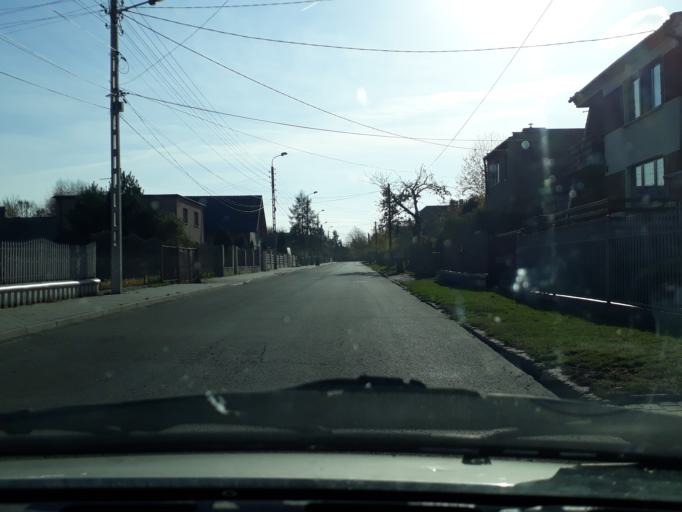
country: PL
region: Silesian Voivodeship
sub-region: Powiat tarnogorski
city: Tarnowskie Gory
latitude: 50.4301
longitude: 18.8441
